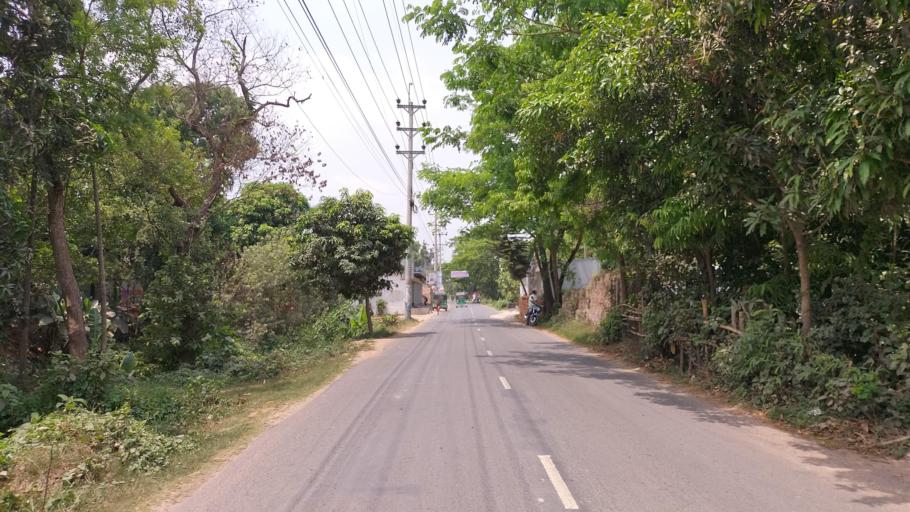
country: BD
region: Dhaka
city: Azimpur
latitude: 23.7295
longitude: 90.2877
